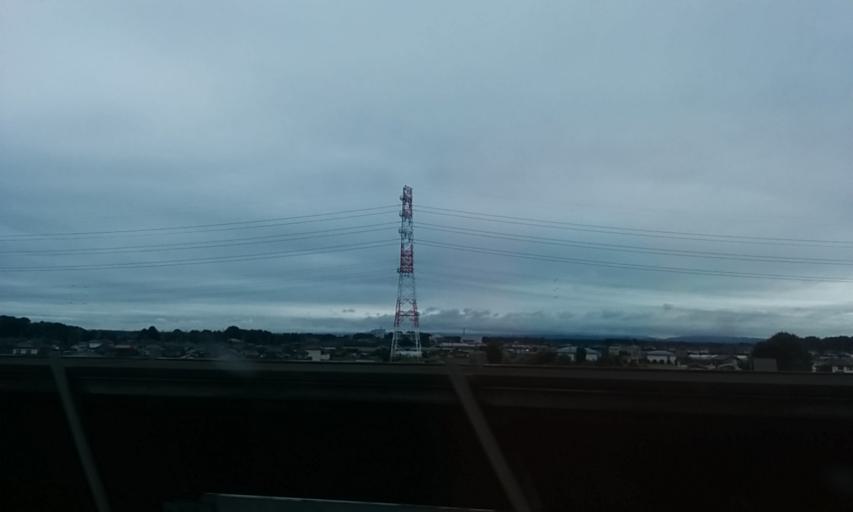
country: JP
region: Tochigi
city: Kaminokawa
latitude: 36.4272
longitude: 139.8651
